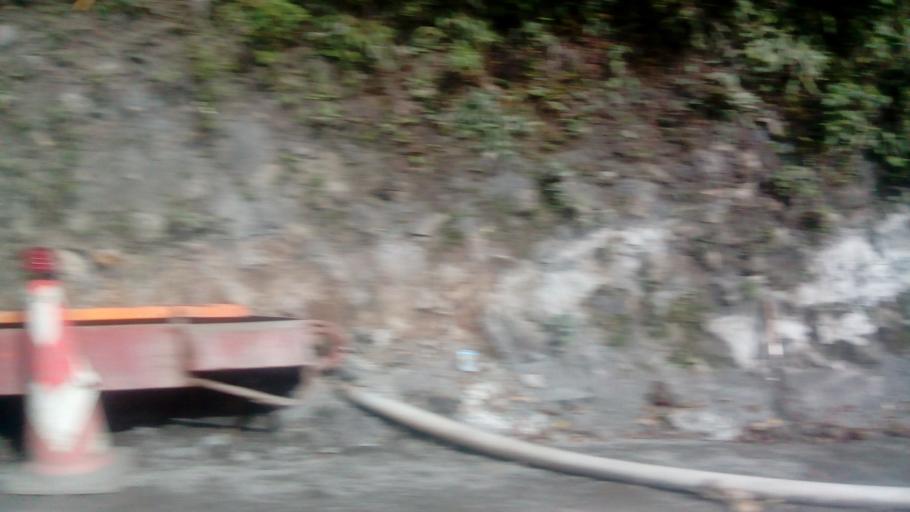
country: TW
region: Taiwan
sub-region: Yilan
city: Yilan
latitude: 24.5703
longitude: 121.4737
